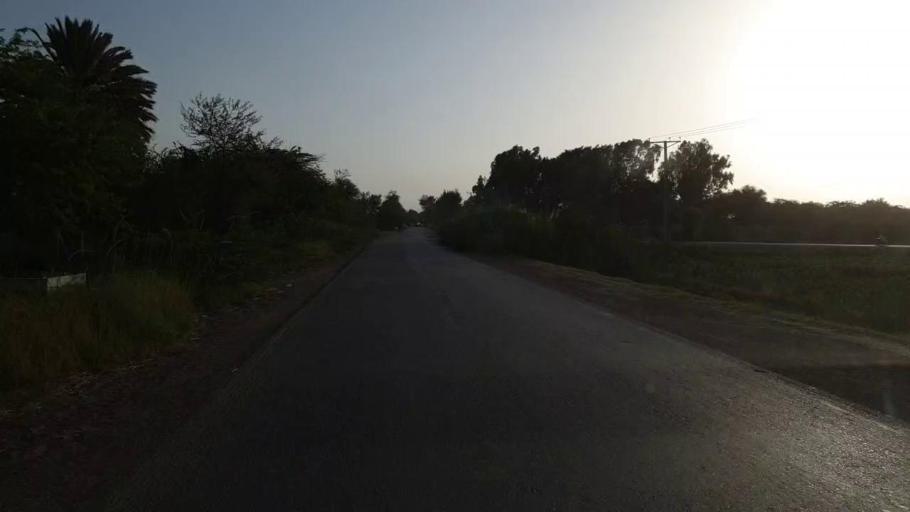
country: PK
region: Sindh
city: Jam Sahib
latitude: 26.2755
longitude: 68.5577
